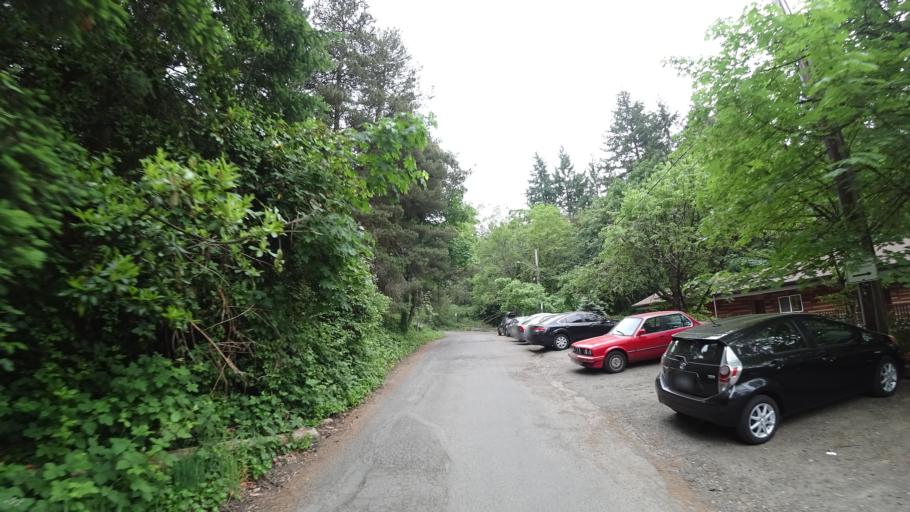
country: US
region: Oregon
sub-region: Multnomah County
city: Portland
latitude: 45.5003
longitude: -122.6932
